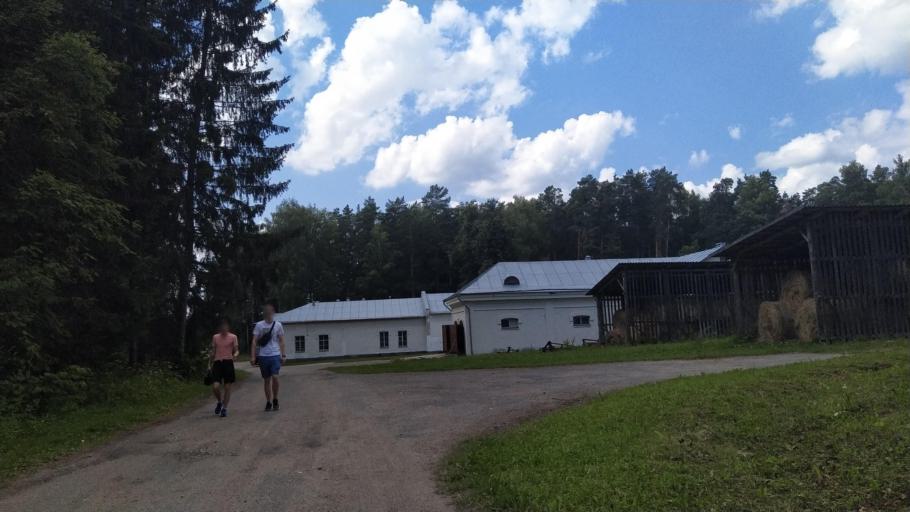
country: RU
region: Pskov
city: Pushkinskiye Gory
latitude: 57.0593
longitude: 28.9341
